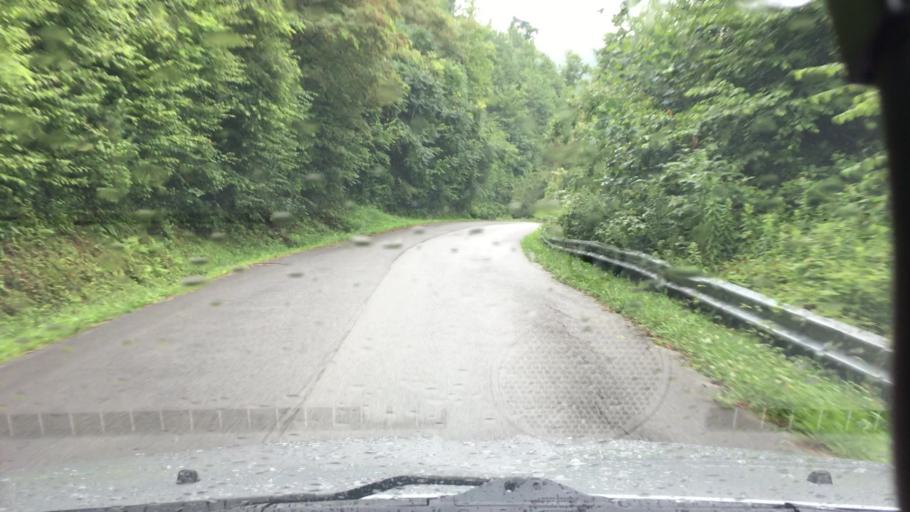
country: US
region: North Carolina
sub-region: Madison County
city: Mars Hill
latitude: 35.9504
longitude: -82.5139
